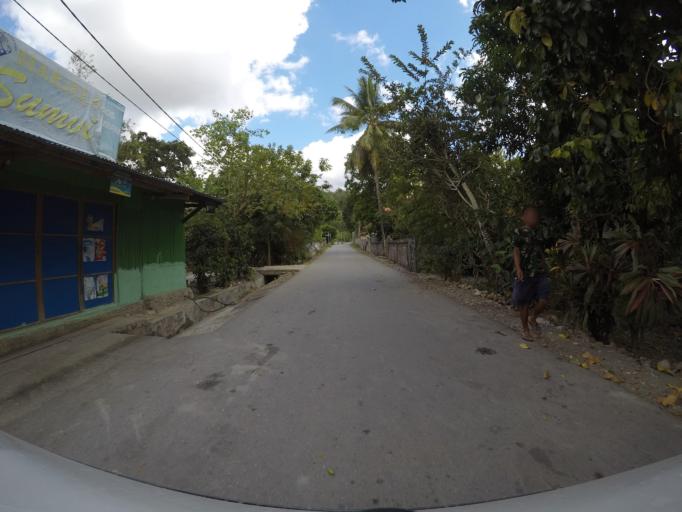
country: TL
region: Viqueque
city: Viqueque
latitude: -8.8707
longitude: 126.3649
